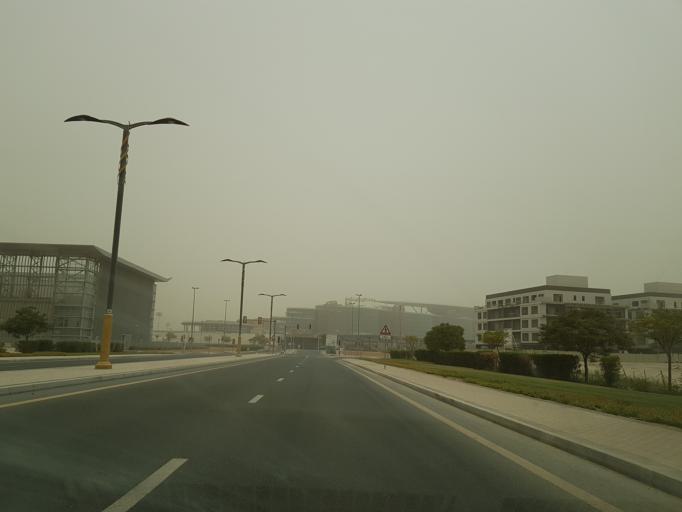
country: AE
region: Dubai
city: Dubai
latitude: 25.1647
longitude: 55.3032
